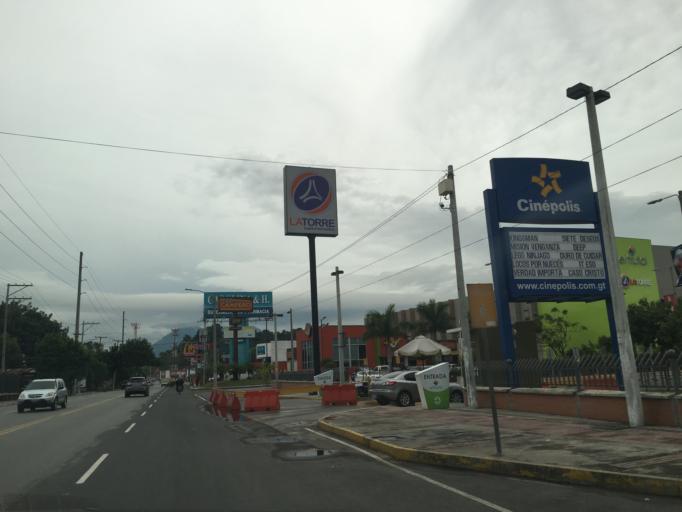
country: GT
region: Guatemala
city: Petapa
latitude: 14.5213
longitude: -90.5637
